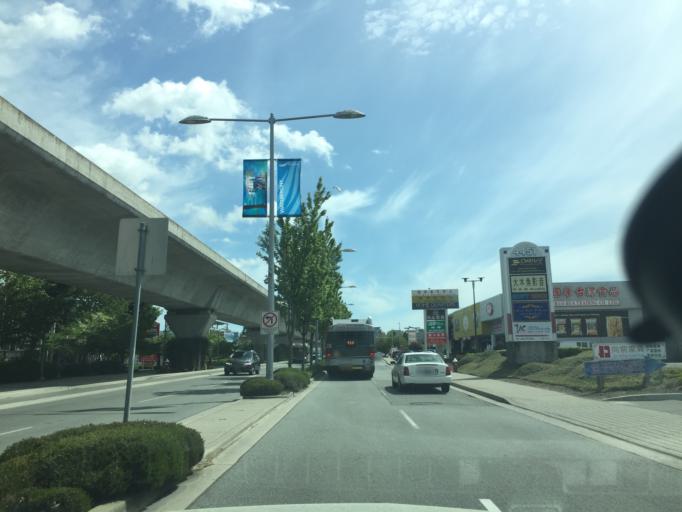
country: CA
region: British Columbia
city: Richmond
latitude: 49.1814
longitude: -123.1369
